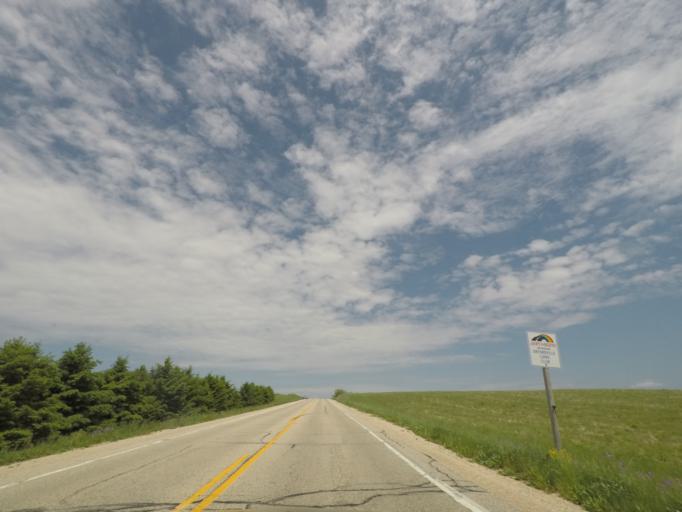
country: US
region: Wisconsin
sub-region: Rock County
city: Orfordville
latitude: 42.6587
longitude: -89.2885
